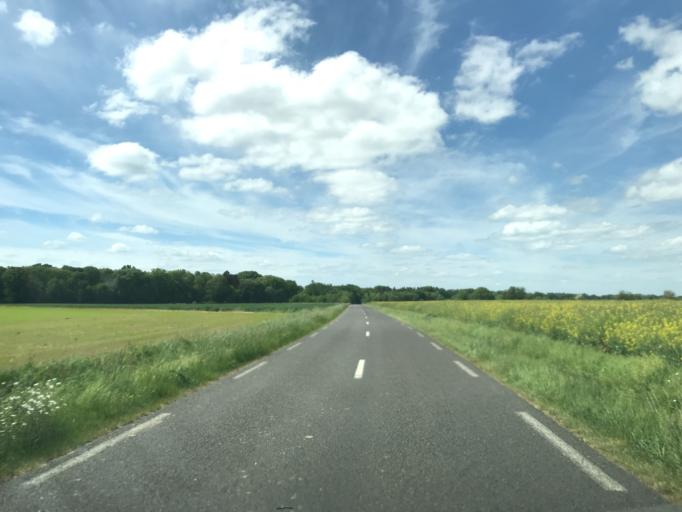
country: FR
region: Haute-Normandie
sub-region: Departement de l'Eure
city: Le Neubourg
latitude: 49.1483
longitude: 0.8269
